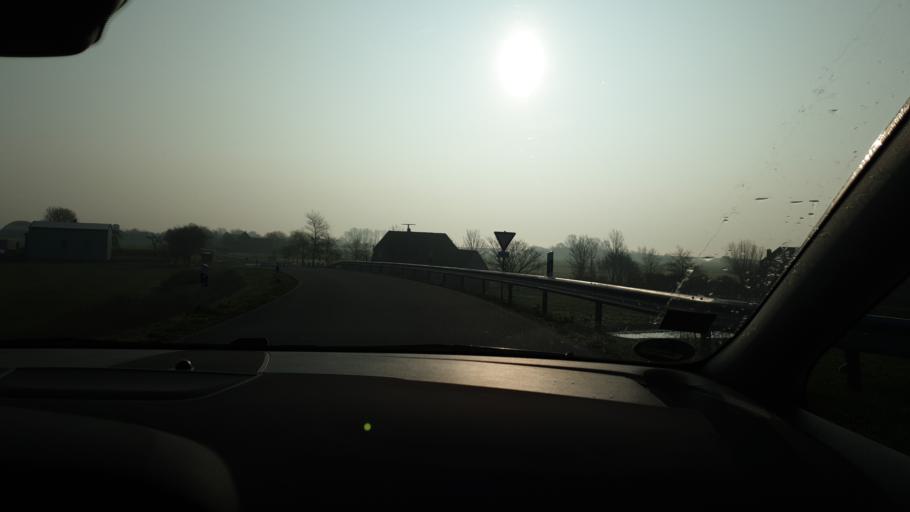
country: DE
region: Schleswig-Holstein
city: Elisabeth-Sophien-Koog
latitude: 54.4960
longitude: 8.9120
